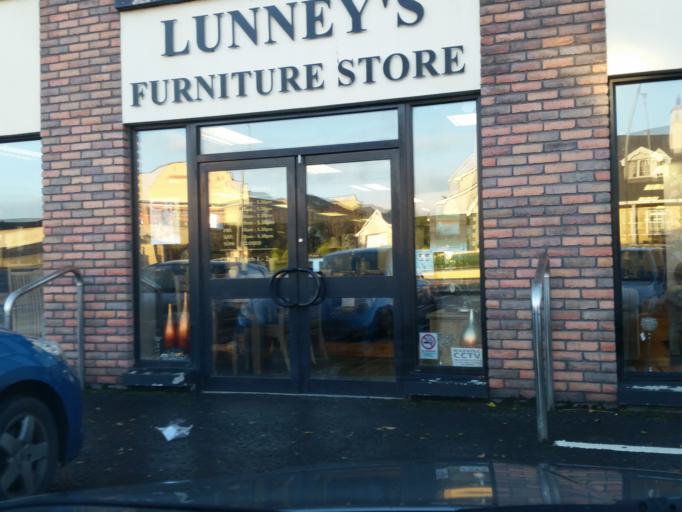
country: IE
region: Ulster
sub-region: An Cabhan
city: Ballyconnell
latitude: 54.1950
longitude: -7.5700
